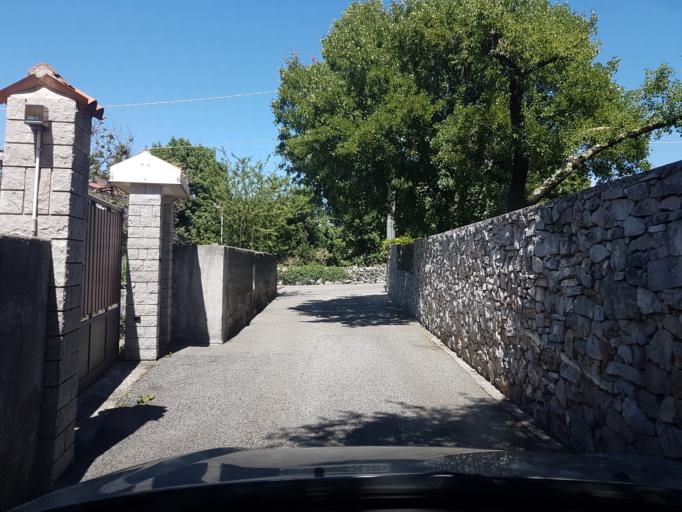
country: IT
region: Friuli Venezia Giulia
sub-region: Provincia di Trieste
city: Villa Opicina
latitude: 45.6918
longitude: 13.7899
